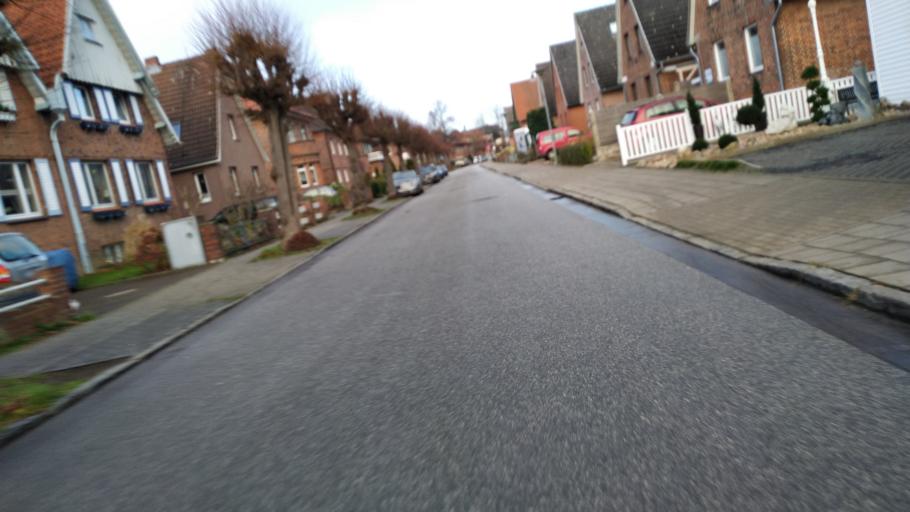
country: DE
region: Schleswig-Holstein
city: Travemuende
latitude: 53.9623
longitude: 10.8714
